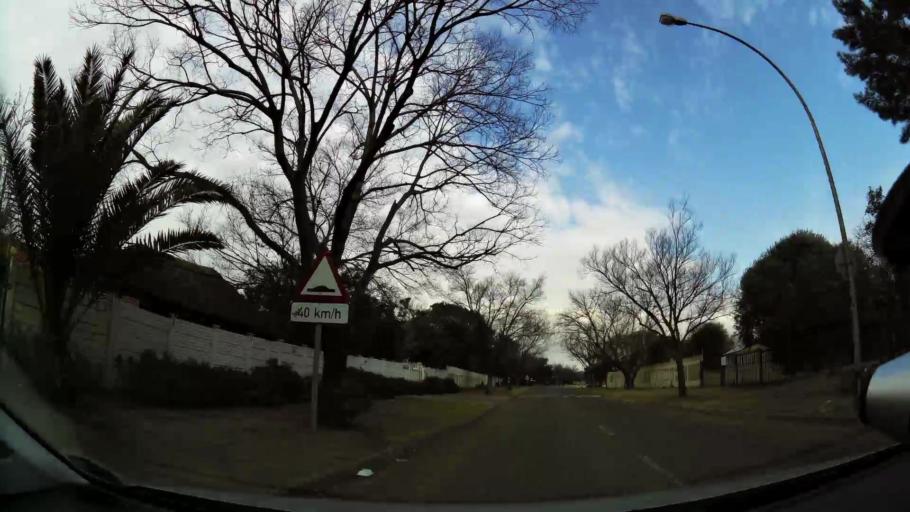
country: ZA
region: Orange Free State
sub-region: Mangaung Metropolitan Municipality
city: Bloemfontein
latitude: -29.1179
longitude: 26.1946
